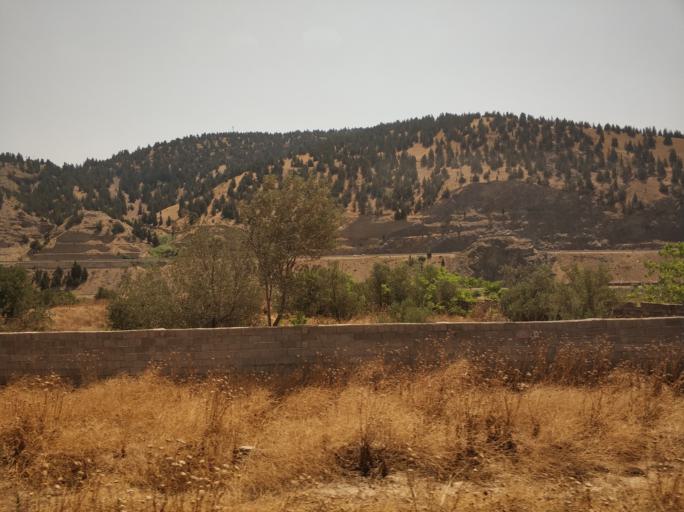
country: IR
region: Gilan
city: Pa'in-e Bazar-e Rudbar
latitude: 36.8516
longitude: 49.4771
